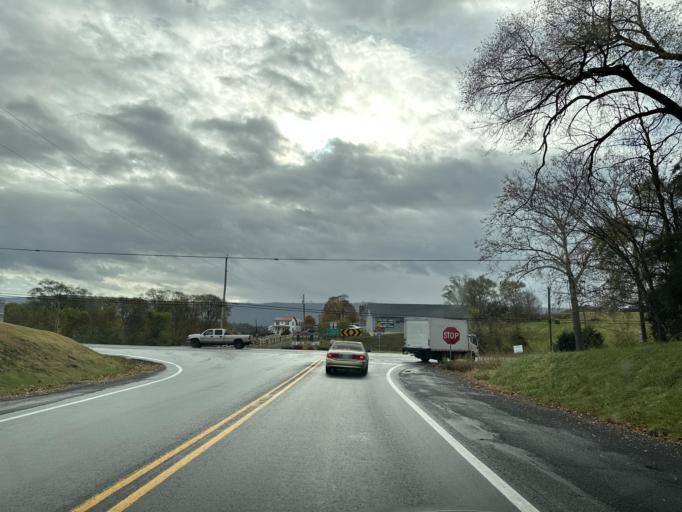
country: US
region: Virginia
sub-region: Shenandoah County
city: Strasburg
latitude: 38.9547
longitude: -78.4287
